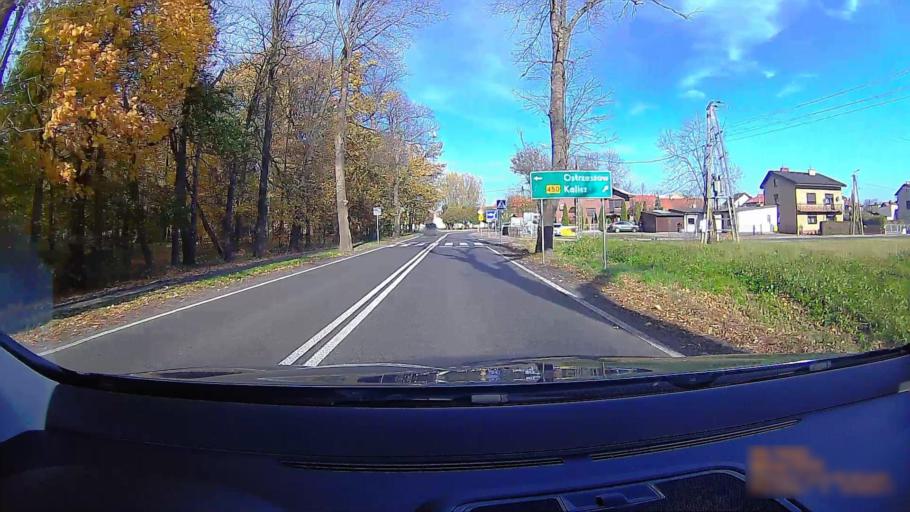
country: PL
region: Greater Poland Voivodeship
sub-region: Powiat ostrzeszowski
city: Doruchow
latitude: 51.4155
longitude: 18.0759
